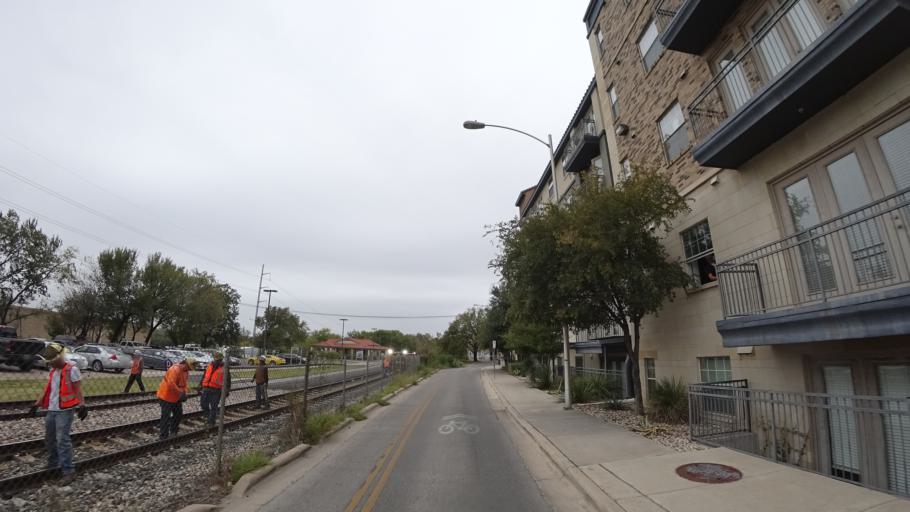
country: US
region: Texas
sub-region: Travis County
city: Austin
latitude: 30.2694
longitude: -97.7559
